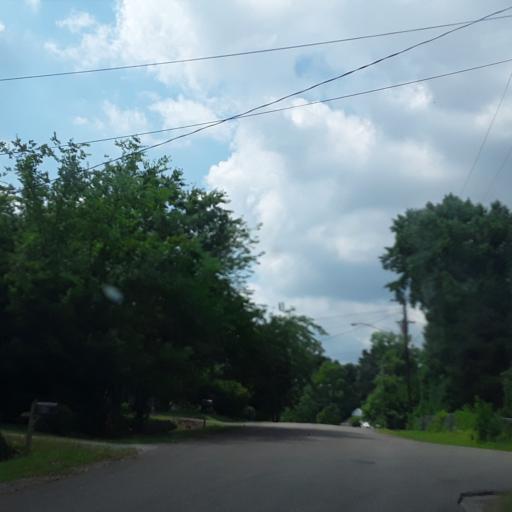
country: US
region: Tennessee
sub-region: Davidson County
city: Oak Hill
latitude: 36.1122
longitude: -86.7318
